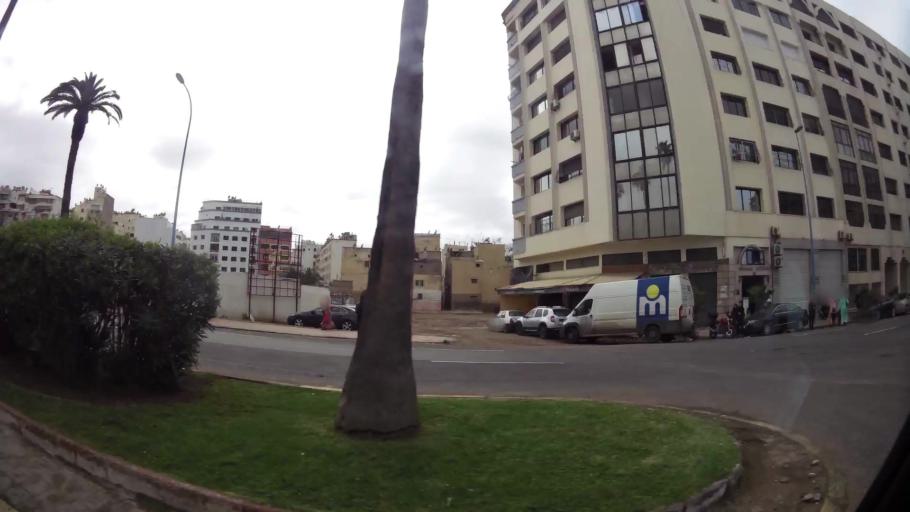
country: MA
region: Grand Casablanca
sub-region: Casablanca
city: Casablanca
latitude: 33.6031
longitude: -7.6331
